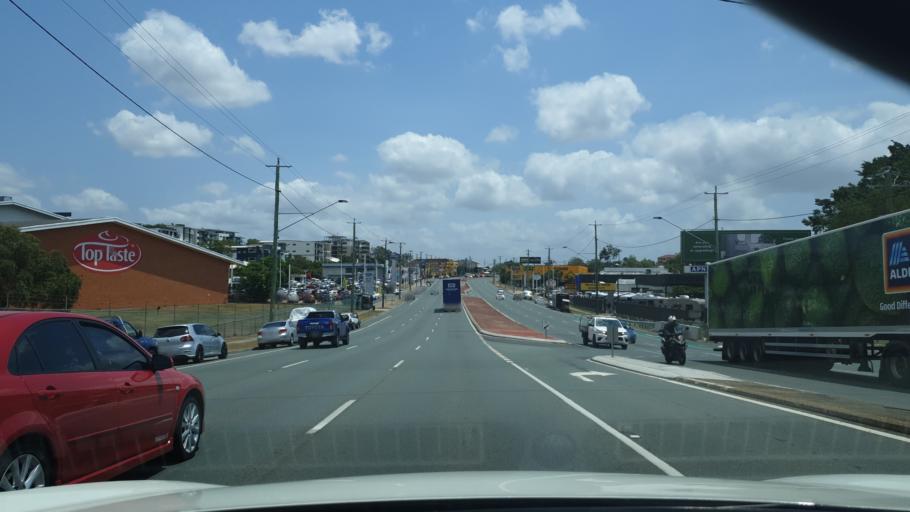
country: AU
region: Queensland
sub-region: Brisbane
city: Wavell Heights
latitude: -27.3981
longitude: 153.0313
